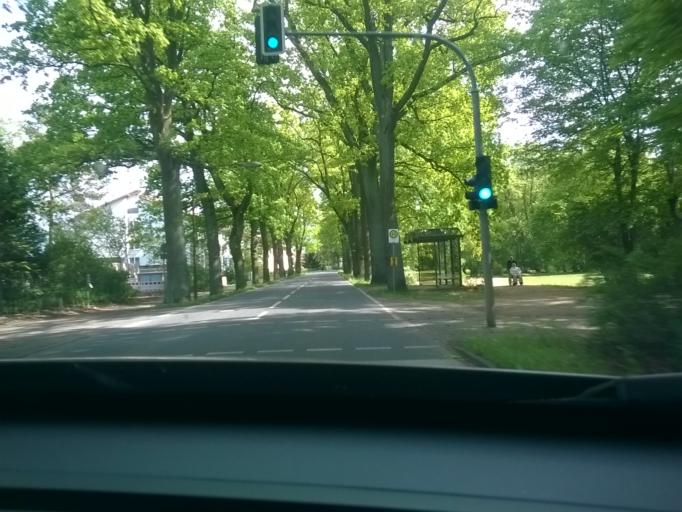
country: DE
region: Brandenburg
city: Wittstock
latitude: 53.1517
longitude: 12.4866
